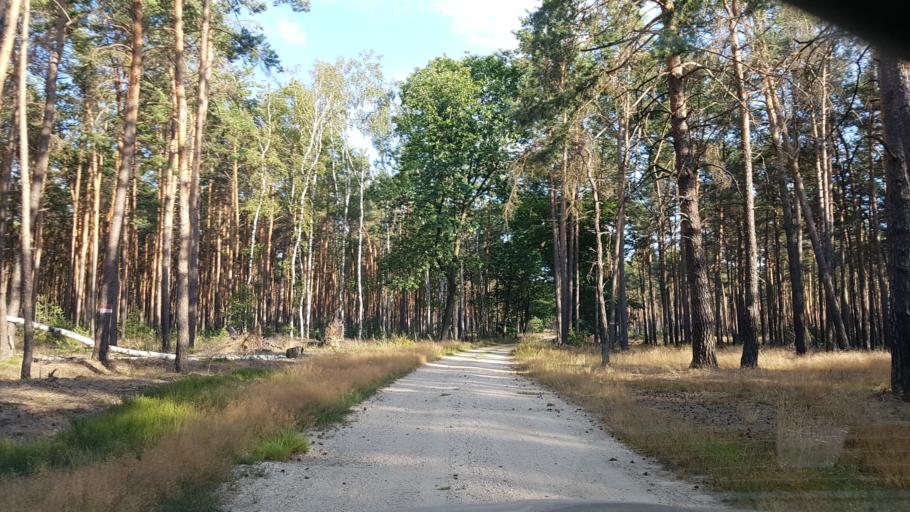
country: DE
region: Brandenburg
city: Trobitz
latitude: 51.6294
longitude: 13.4085
